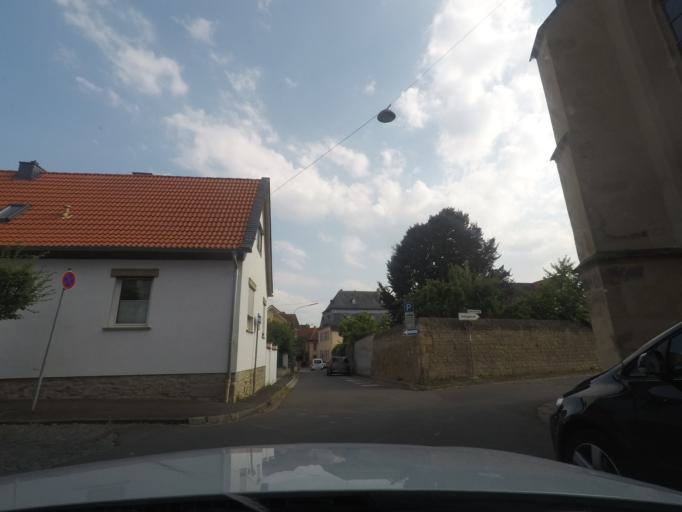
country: DE
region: Rheinland-Pfalz
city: Staudernheim
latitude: 49.7864
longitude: 7.6514
